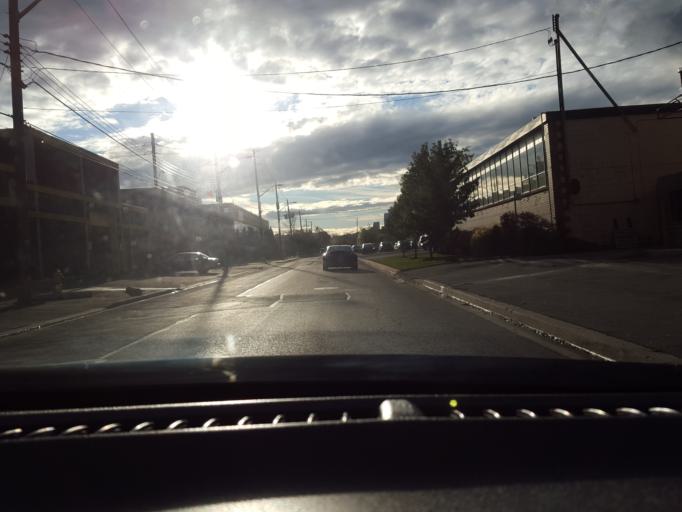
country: CA
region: Ontario
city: Toronto
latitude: 43.7124
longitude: -79.3530
